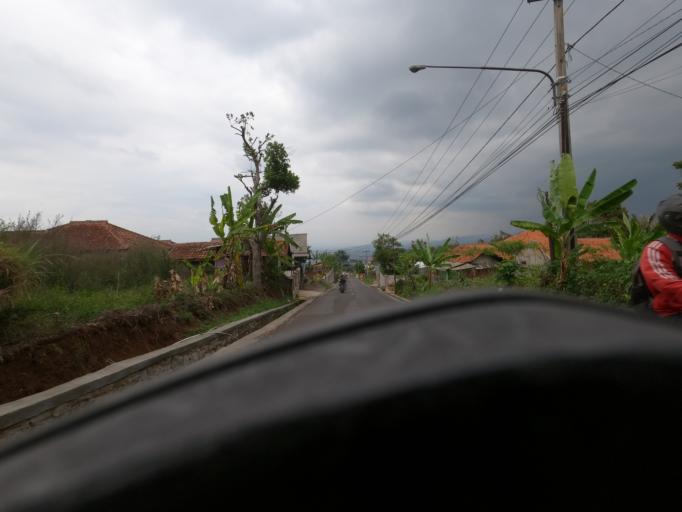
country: ID
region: West Java
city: Padalarang
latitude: -6.8337
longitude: 107.5171
